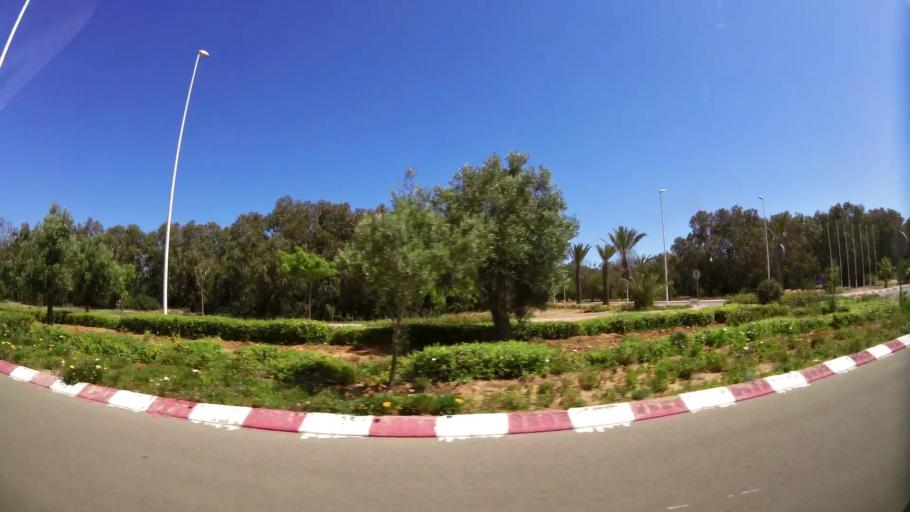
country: MA
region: Oriental
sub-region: Berkane-Taourirt
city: Madagh
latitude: 35.0996
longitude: -2.2835
